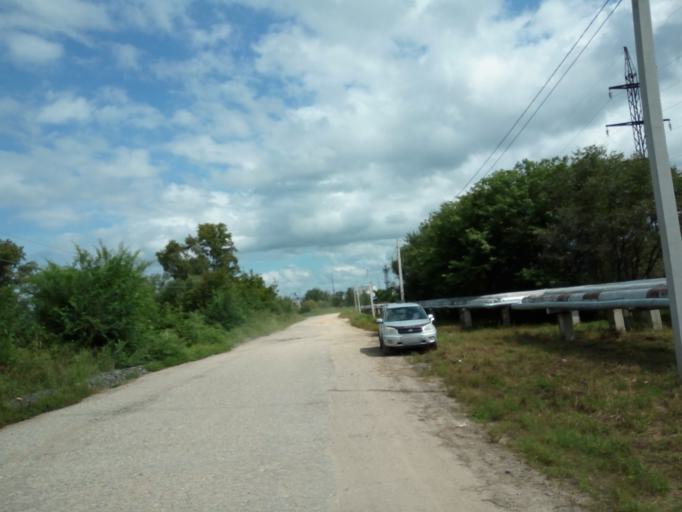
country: RU
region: Primorskiy
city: Dal'nerechensk
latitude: 45.9506
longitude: 133.8199
